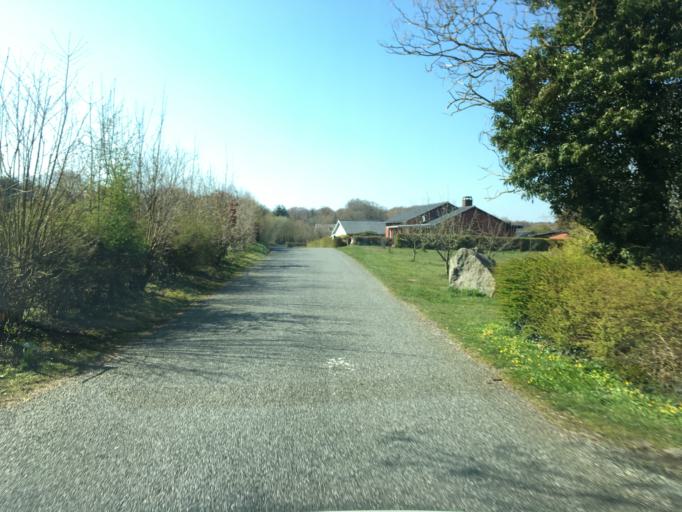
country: DK
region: South Denmark
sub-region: Aabenraa Kommune
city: Krusa
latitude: 54.9252
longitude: 9.4443
